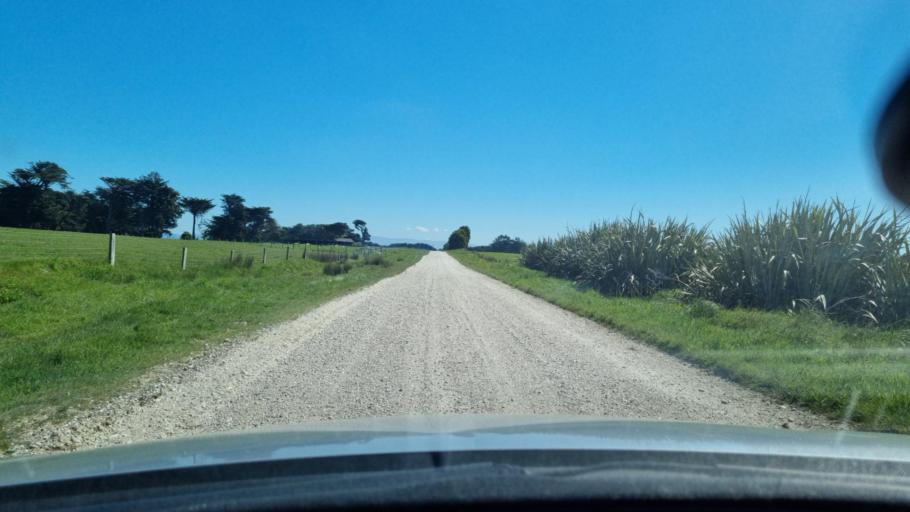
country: NZ
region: Southland
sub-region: Invercargill City
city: Invercargill
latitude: -46.4192
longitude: 168.2707
